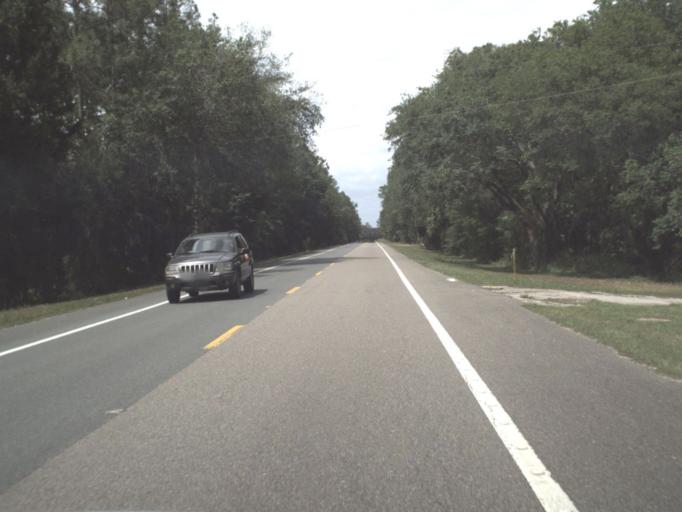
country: US
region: Florida
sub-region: Flagler County
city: Bunnell
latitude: 29.3611
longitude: -81.3115
